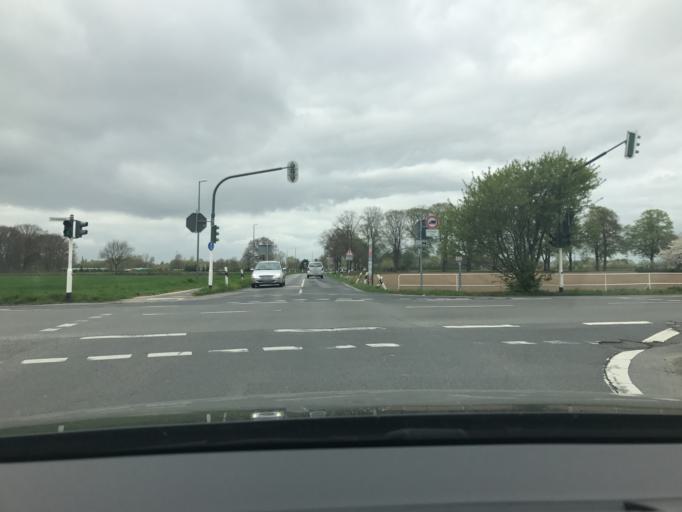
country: DE
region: North Rhine-Westphalia
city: Tonisvorst
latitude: 51.3061
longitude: 6.5250
